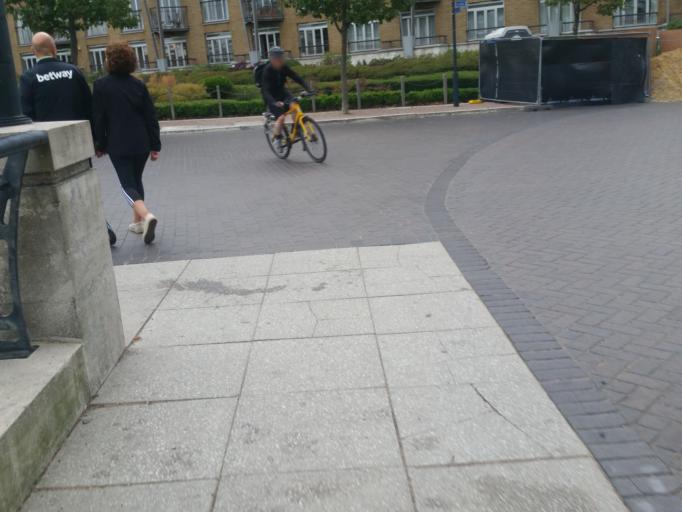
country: GB
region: England
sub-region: Greater London
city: Poplar
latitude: 51.5074
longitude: -0.0298
